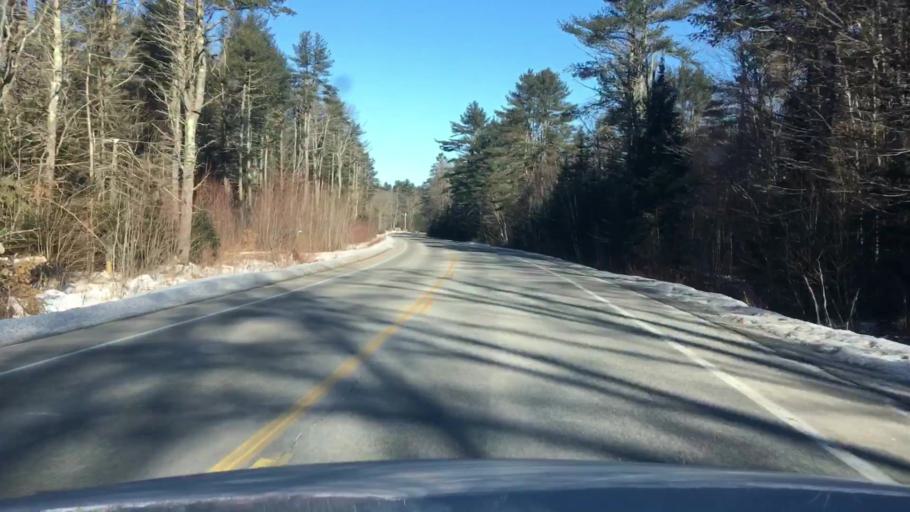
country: US
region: Maine
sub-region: Androscoggin County
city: Lisbon Falls
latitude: 43.9555
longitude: -70.1216
